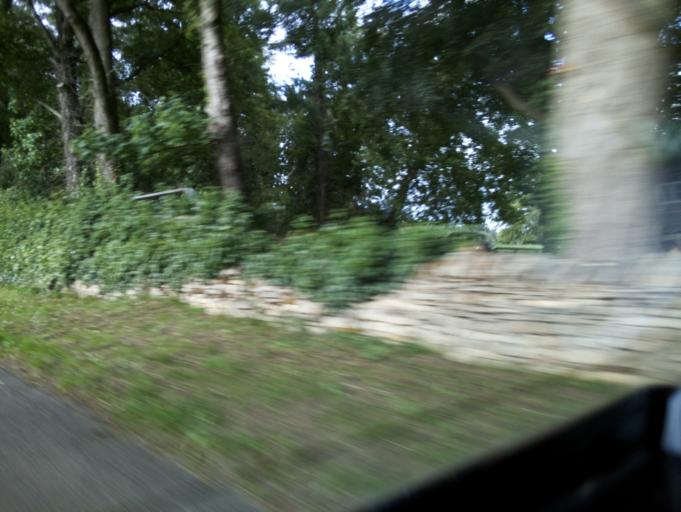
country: GB
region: England
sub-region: Gloucestershire
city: Donnington
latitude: 51.9812
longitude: -1.7552
